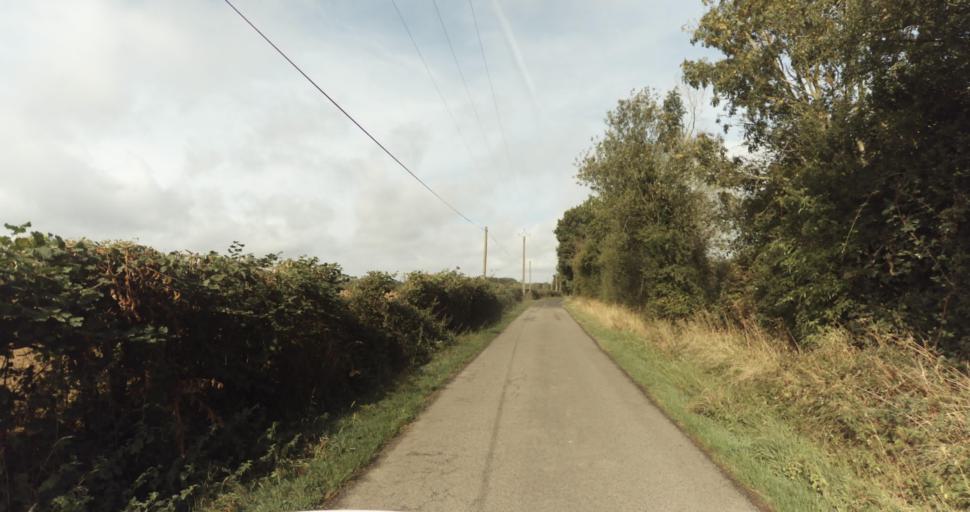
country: FR
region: Lower Normandy
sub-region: Departement de l'Orne
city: Gace
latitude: 48.8610
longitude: 0.3327
